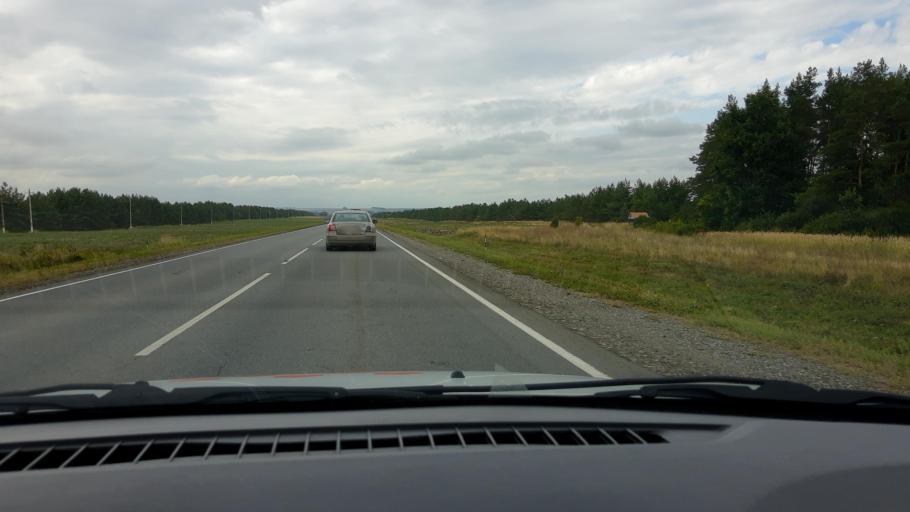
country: RU
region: Tatarstan
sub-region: Alekseyevskiy Rayon
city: Alekseyevskoye
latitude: 55.3099
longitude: 50.3387
